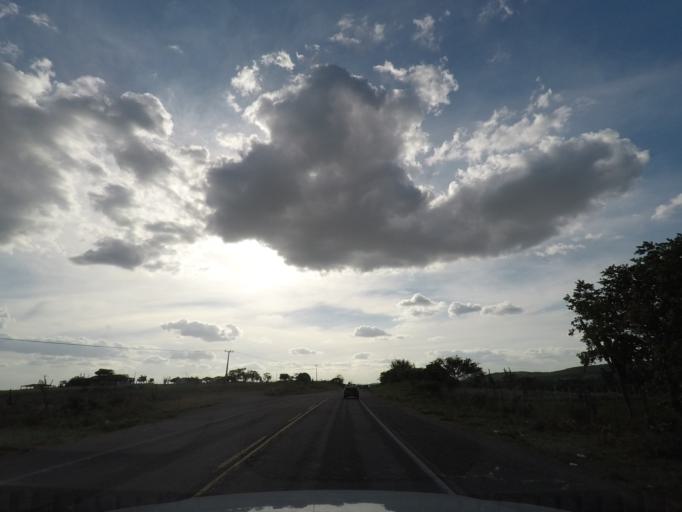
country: BR
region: Bahia
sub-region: Anguera
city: Anguera
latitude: -12.1867
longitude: -39.4872
